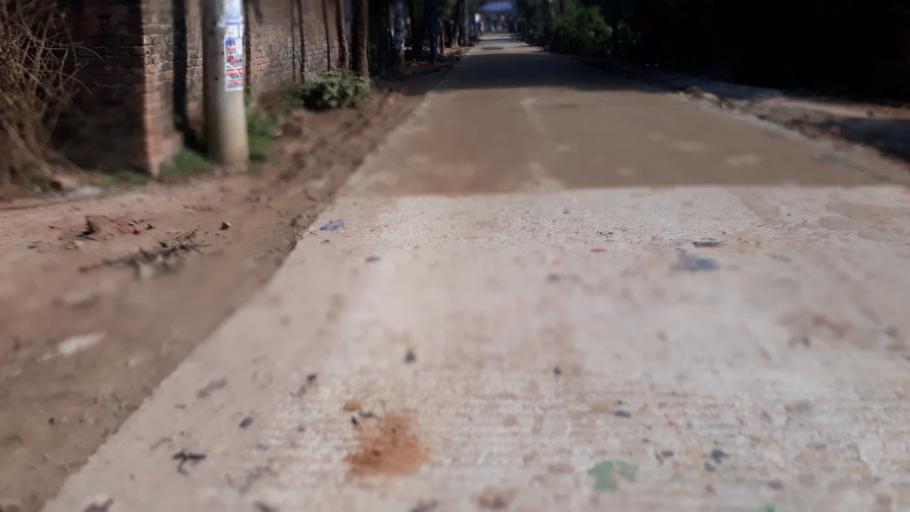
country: BD
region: Dhaka
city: Tungi
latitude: 23.8544
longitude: 90.2984
